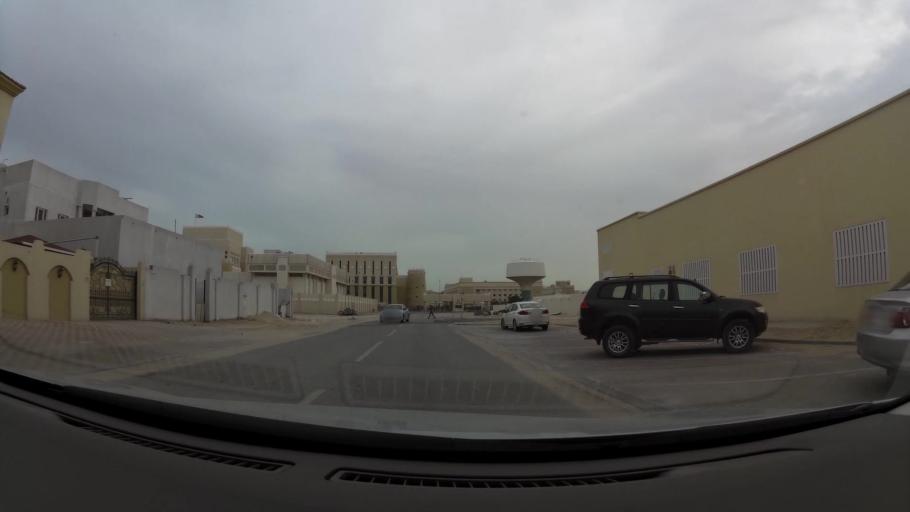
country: QA
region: Baladiyat ad Dawhah
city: Doha
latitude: 25.3076
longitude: 51.5016
